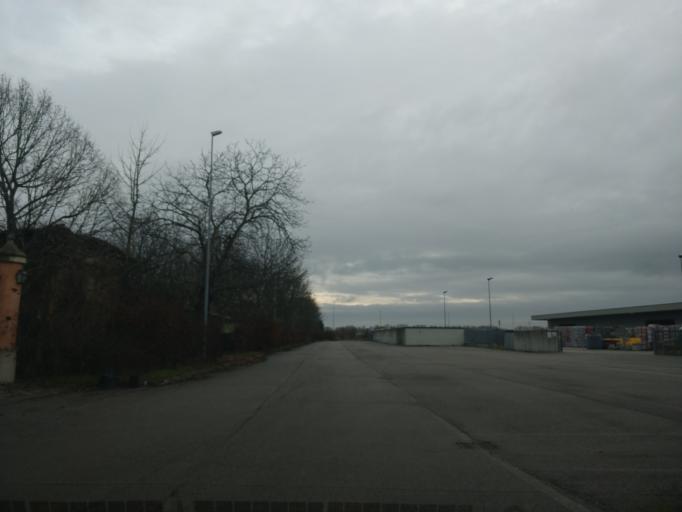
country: IT
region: Emilia-Romagna
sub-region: Provincia di Ferrara
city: Corpo Reno
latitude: 44.7525
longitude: 11.3042
